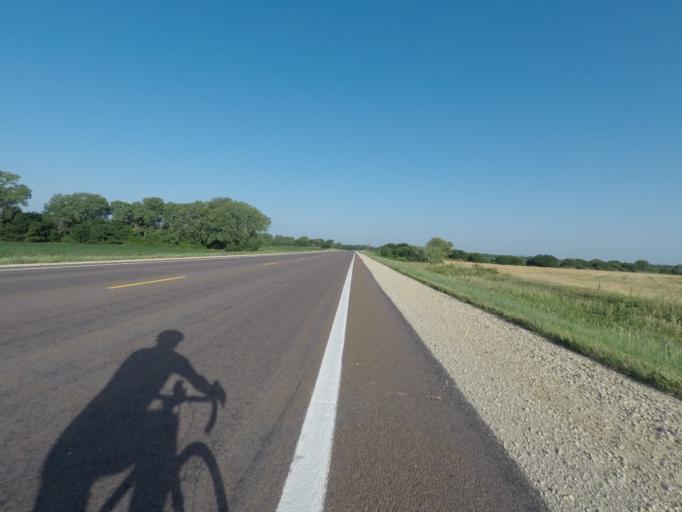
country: US
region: Kansas
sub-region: Riley County
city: Fort Riley North
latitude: 39.3044
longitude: -96.8441
